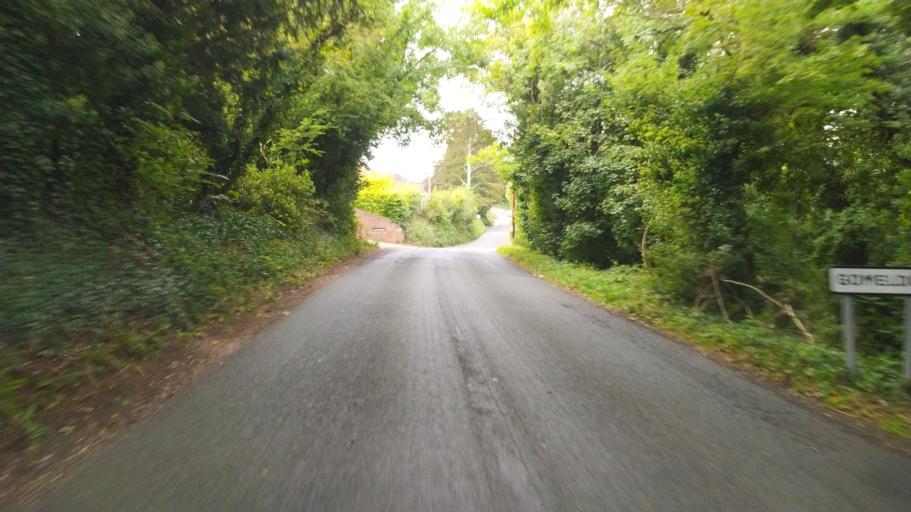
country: GB
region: England
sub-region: Wiltshire
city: Allington
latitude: 51.1231
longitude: -1.7354
